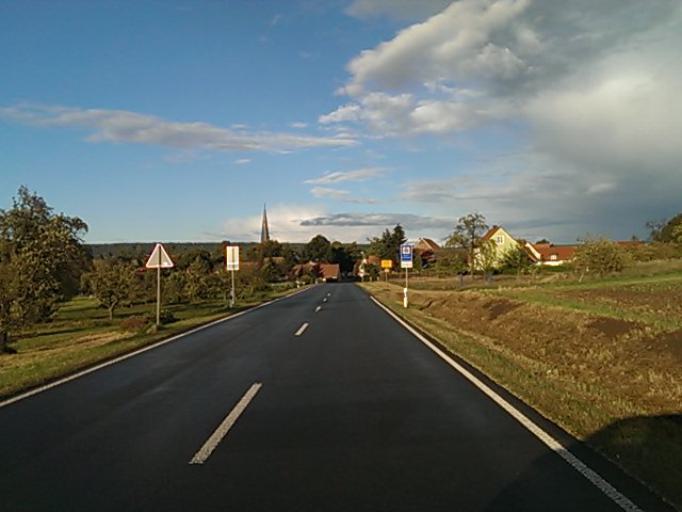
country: DE
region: Thuringia
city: Grossmonra
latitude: 51.1975
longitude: 11.2813
